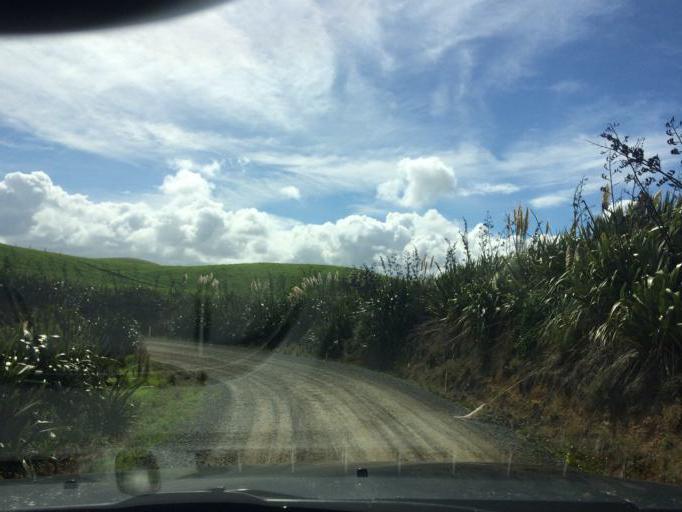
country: NZ
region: Northland
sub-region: Kaipara District
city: Dargaville
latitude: -35.9720
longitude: 173.7806
